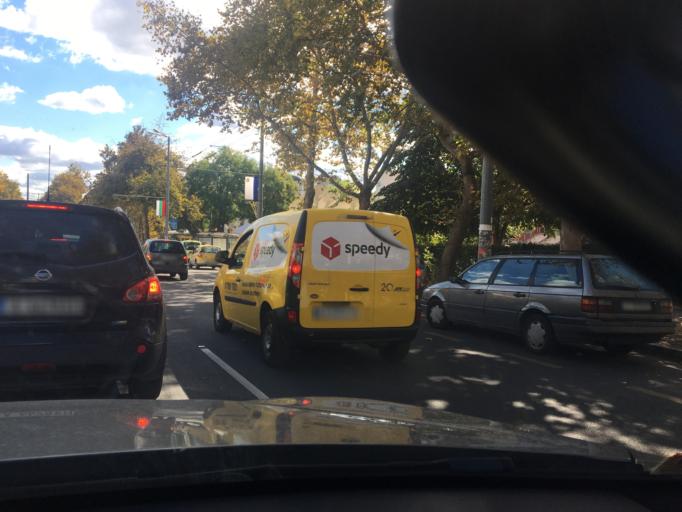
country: BG
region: Burgas
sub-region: Obshtina Burgas
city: Burgas
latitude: 42.5043
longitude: 27.4697
